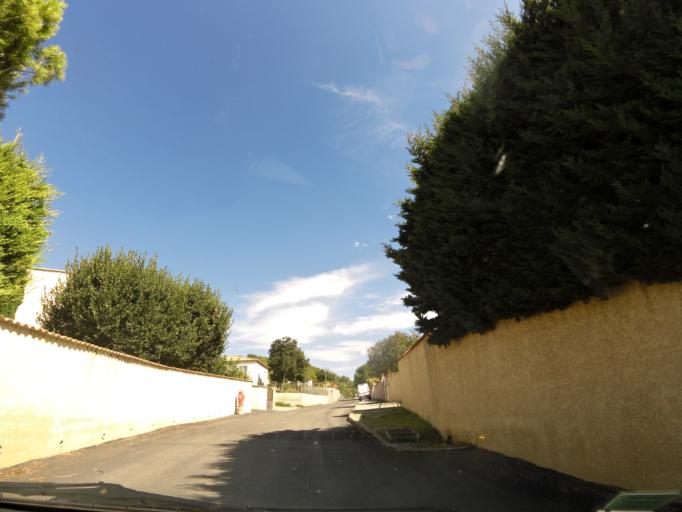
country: FR
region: Languedoc-Roussillon
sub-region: Departement du Gard
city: Nages-et-Solorgues
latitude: 43.7875
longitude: 4.2349
